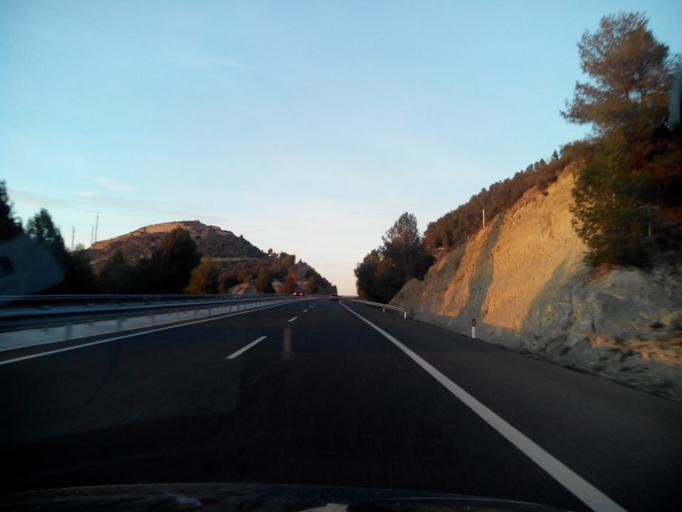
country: ES
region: Catalonia
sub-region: Provincia de Barcelona
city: Monistrol de Montserrat
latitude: 41.6684
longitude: 1.8762
